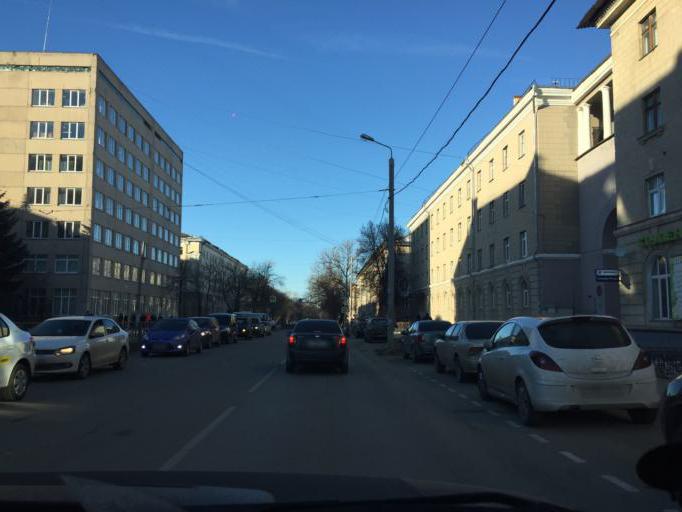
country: RU
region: Tula
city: Mendeleyevskiy
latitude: 54.1673
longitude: 37.5876
